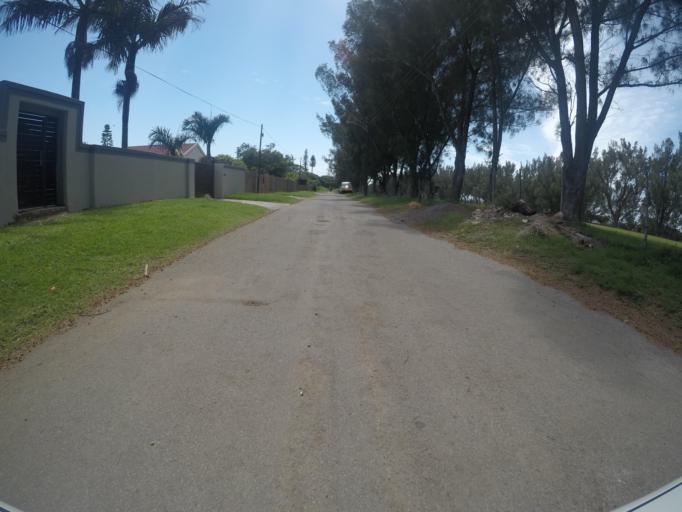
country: ZA
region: Eastern Cape
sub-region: Buffalo City Metropolitan Municipality
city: East London
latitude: -32.9530
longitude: 27.9999
